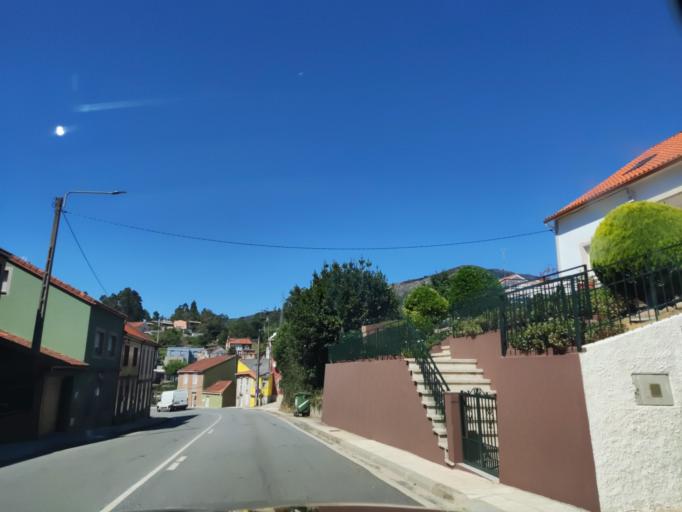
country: ES
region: Galicia
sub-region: Provincia da Coruna
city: Boiro
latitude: 42.6175
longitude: -8.9310
